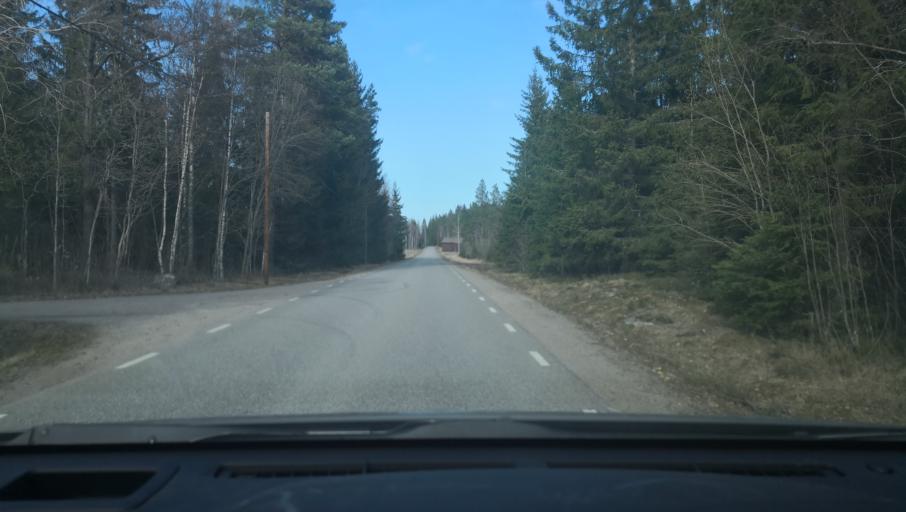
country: SE
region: Uppsala
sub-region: Heby Kommun
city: Heby
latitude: 59.9122
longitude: 16.8286
